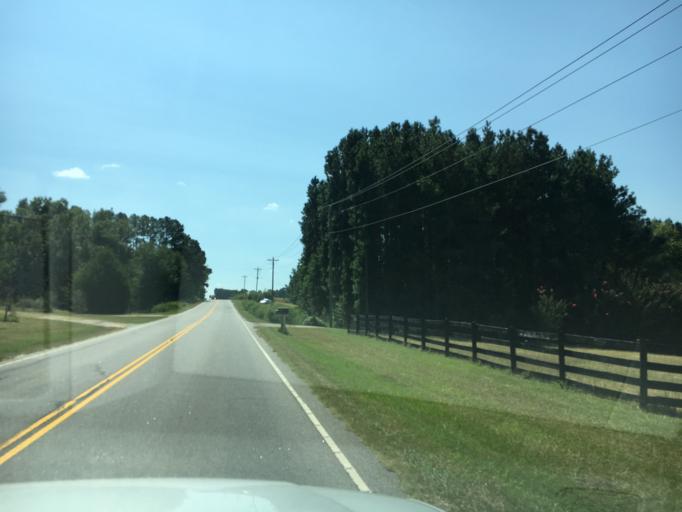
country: US
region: South Carolina
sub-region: Saluda County
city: Saluda
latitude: 33.9061
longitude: -81.7022
